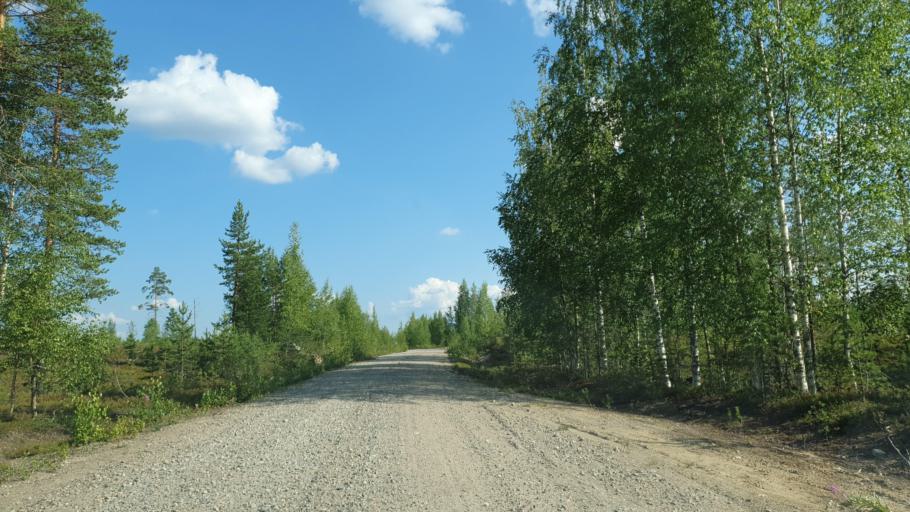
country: FI
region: Kainuu
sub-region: Kehys-Kainuu
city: Kuhmo
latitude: 63.9514
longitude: 29.5689
